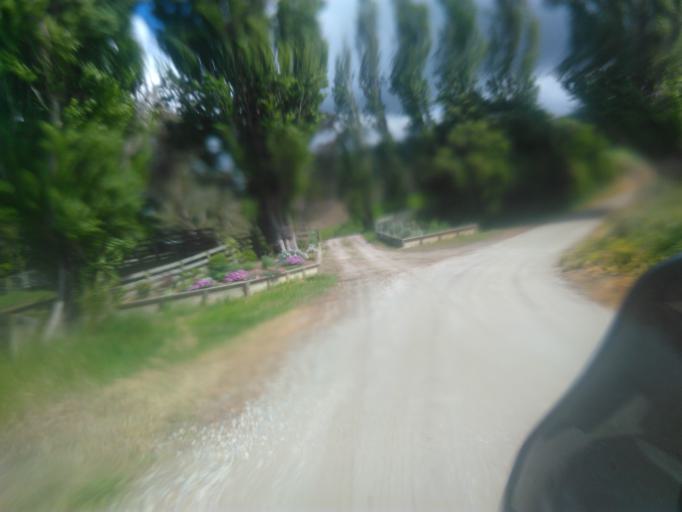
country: NZ
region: Hawke's Bay
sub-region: Wairoa District
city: Wairoa
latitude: -38.7607
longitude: 177.5956
